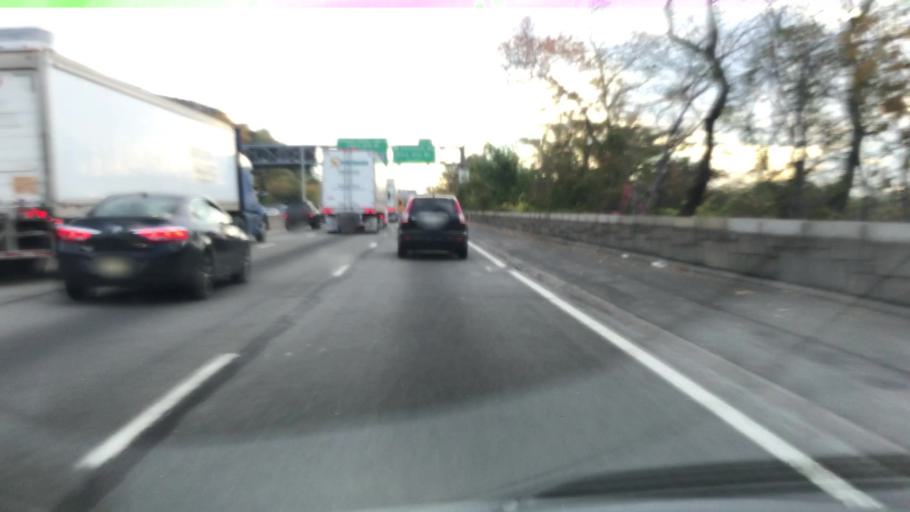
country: US
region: New York
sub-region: New York County
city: Inwood
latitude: 40.8717
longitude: -73.9069
